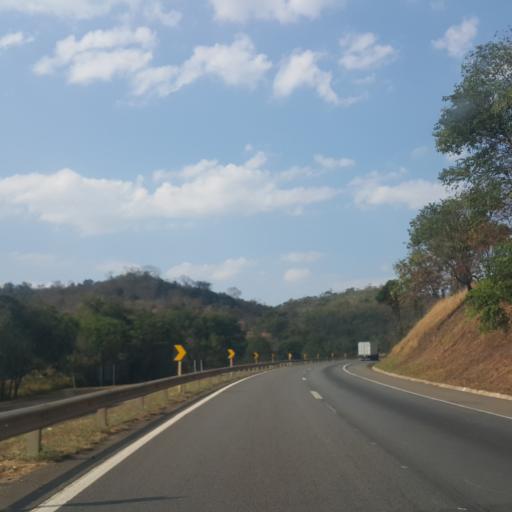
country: BR
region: Goias
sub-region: Abadiania
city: Abadiania
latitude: -16.1110
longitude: -48.5855
